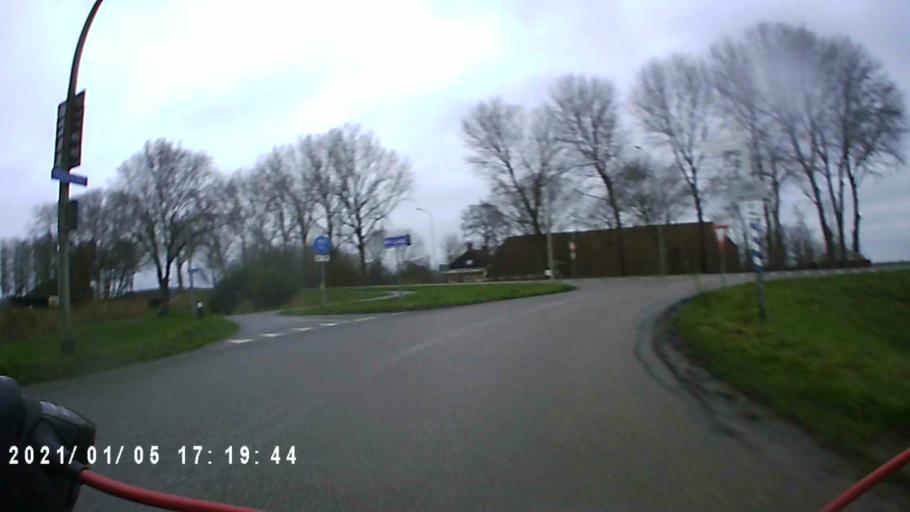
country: NL
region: Groningen
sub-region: Gemeente Delfzijl
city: Delfzijl
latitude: 53.2365
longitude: 6.9644
